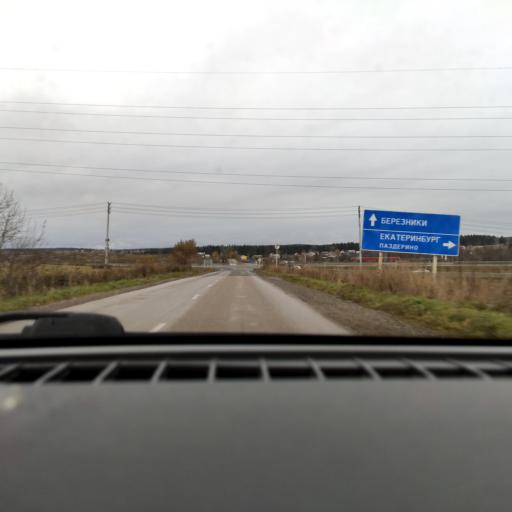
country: RU
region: Perm
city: Ferma
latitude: 57.9291
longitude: 56.3303
